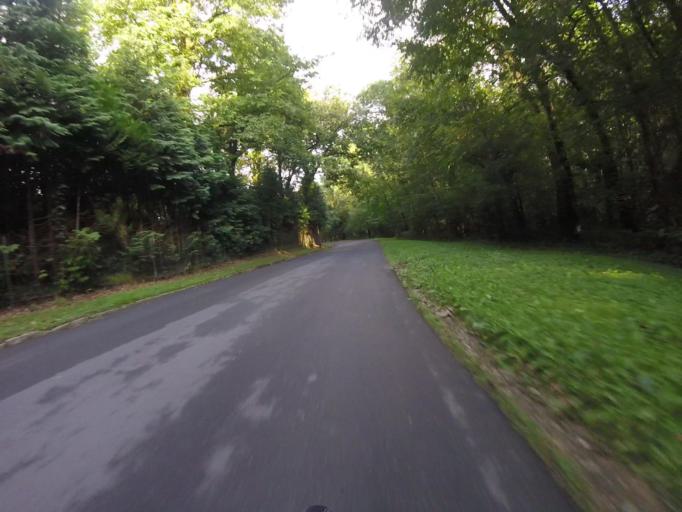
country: ES
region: Basque Country
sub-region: Provincia de Guipuzcoa
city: Irun
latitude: 43.3409
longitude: -1.8269
